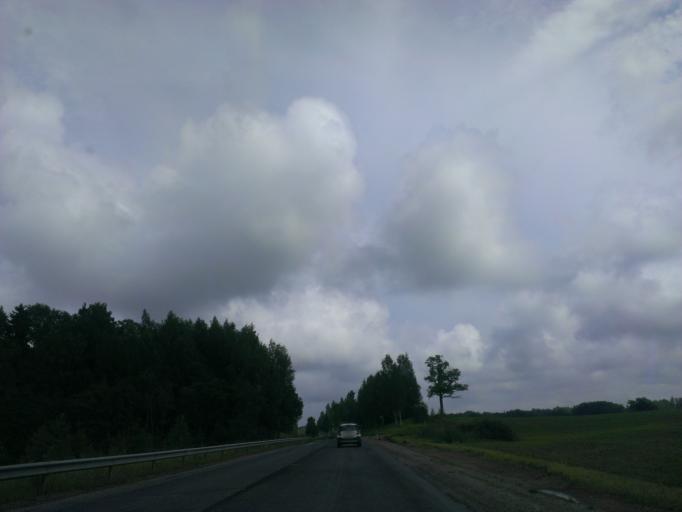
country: LV
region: Ligatne
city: Ligatne
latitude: 57.2041
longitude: 25.1395
